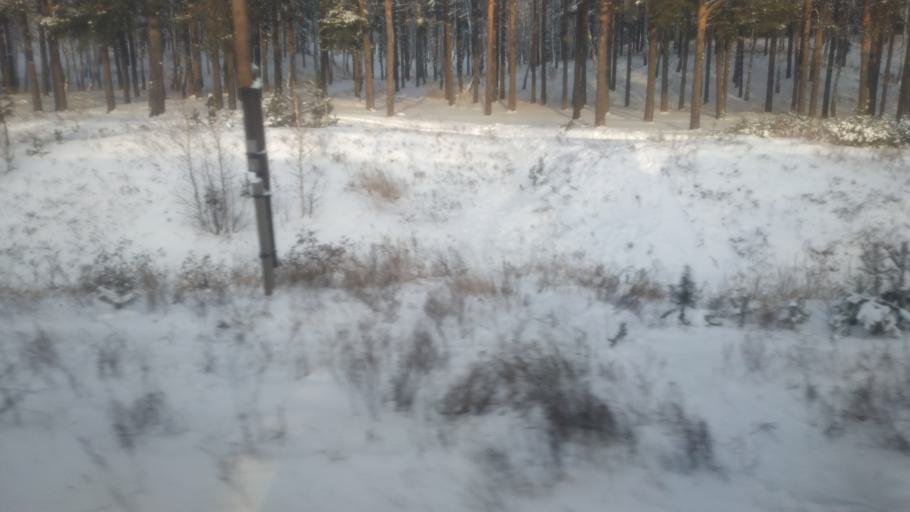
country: RU
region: Kirov
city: Krasnaya Polyana
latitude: 56.2488
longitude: 51.1560
